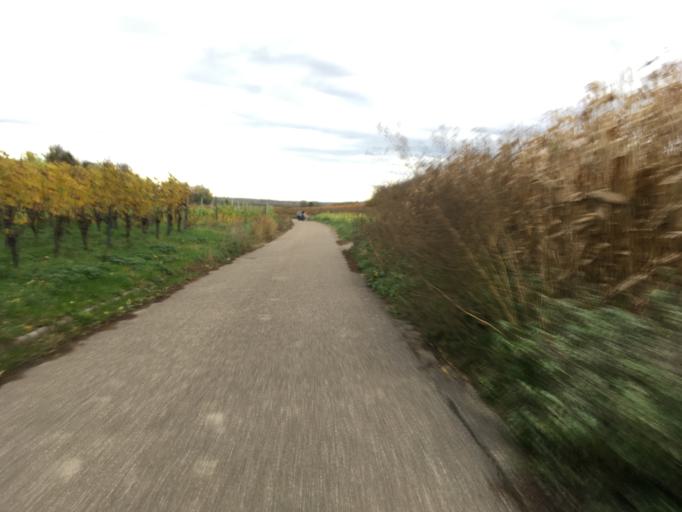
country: DE
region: Baden-Wuerttemberg
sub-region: Freiburg Region
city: Gottenheim
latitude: 48.0325
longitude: 7.7182
